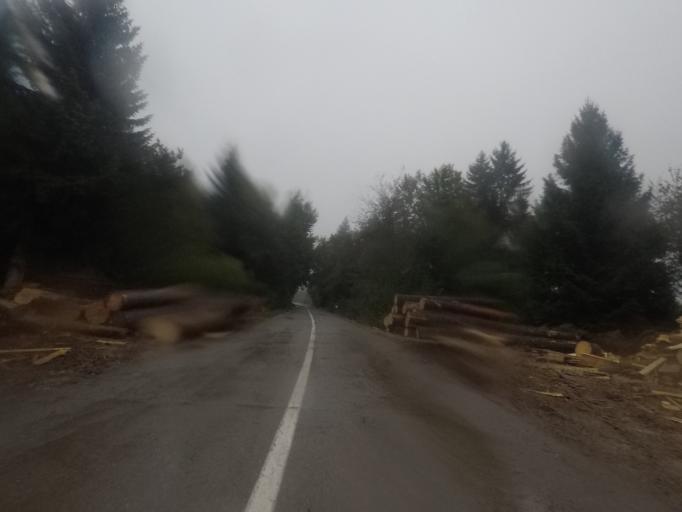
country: HR
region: Licko-Senjska
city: Jezerce
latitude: 44.9551
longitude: 15.5274
